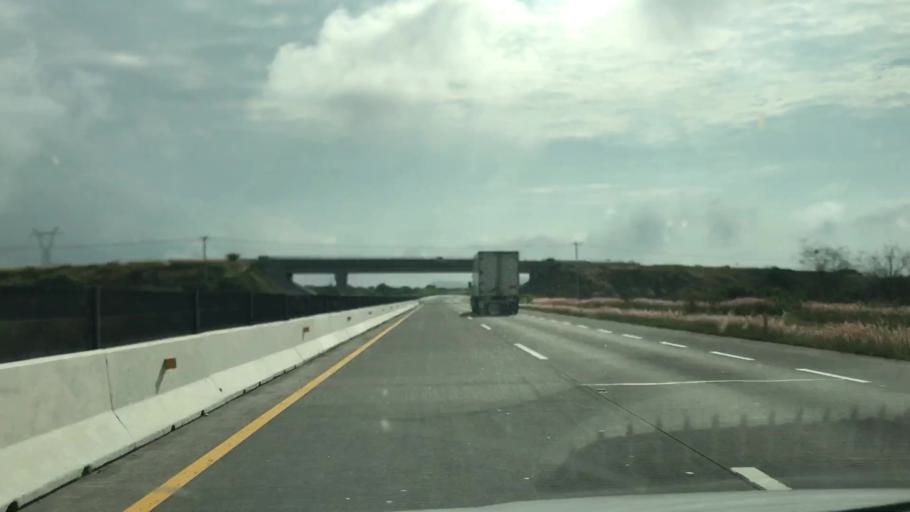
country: MX
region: Michoacan
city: La Piedad Cavadas
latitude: 20.4012
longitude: -102.0425
